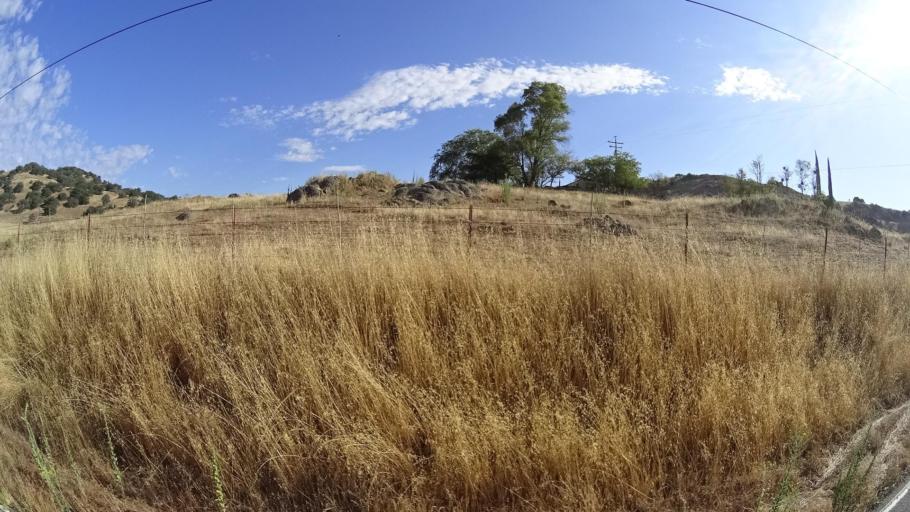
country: US
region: California
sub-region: San Diego County
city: Julian
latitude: 33.1601
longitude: -116.7232
